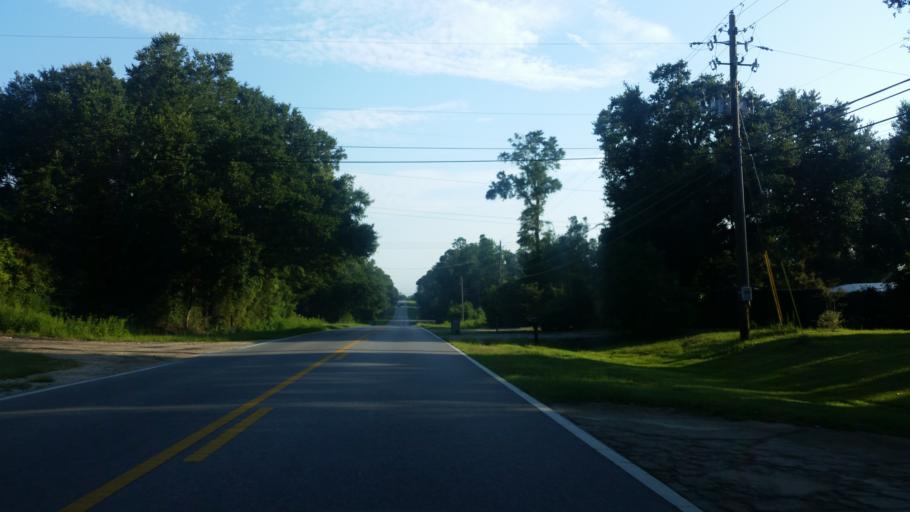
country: US
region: Florida
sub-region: Escambia County
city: Gonzalez
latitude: 30.5812
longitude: -87.2609
